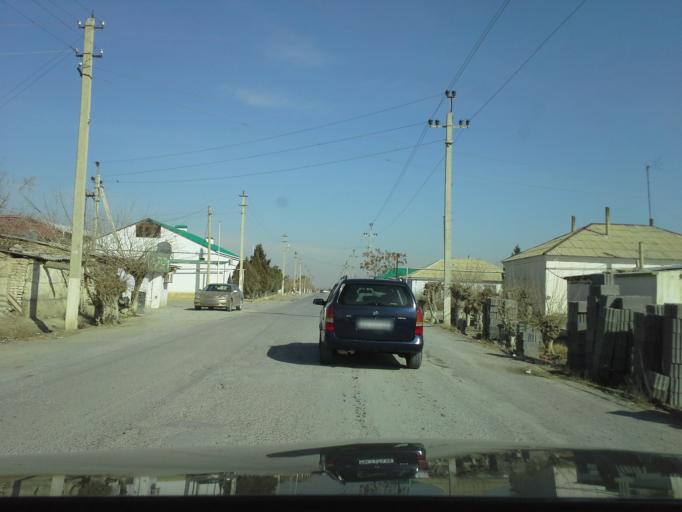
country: TM
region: Ahal
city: Abadan
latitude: 38.1260
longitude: 57.9994
